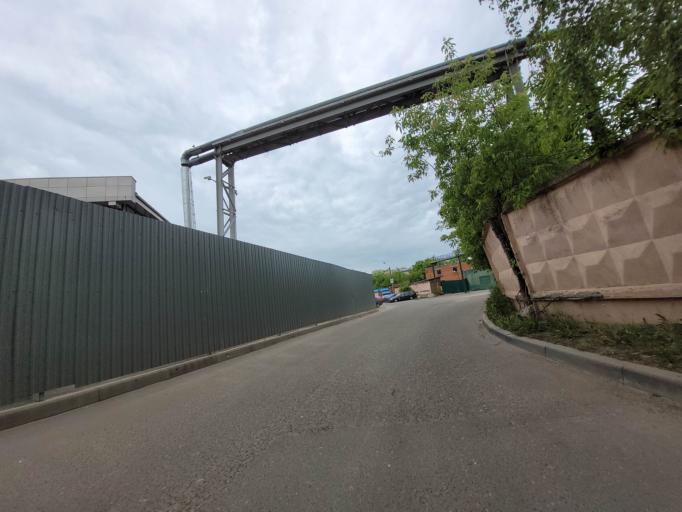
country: RU
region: Moskovskaya
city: Yubileyny
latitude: 55.9435
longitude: 37.8478
